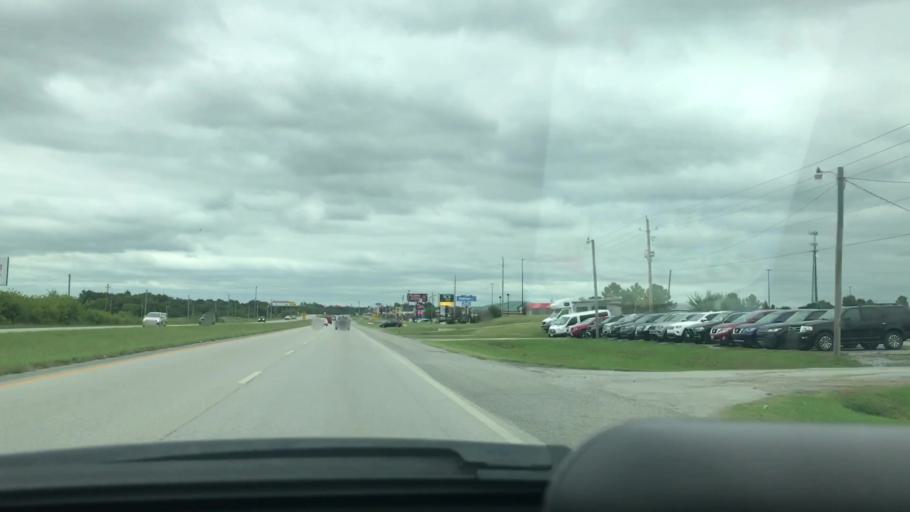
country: US
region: Oklahoma
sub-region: Mayes County
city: Pryor
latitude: 36.2602
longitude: -95.3338
